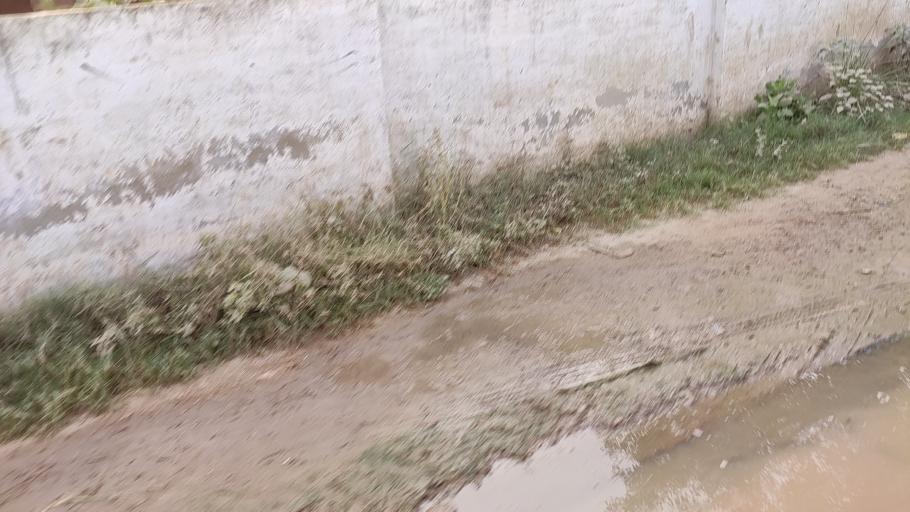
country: IN
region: Uttar Pradesh
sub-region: Mathura
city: Vrindavan
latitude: 27.5449
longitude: 77.7109
